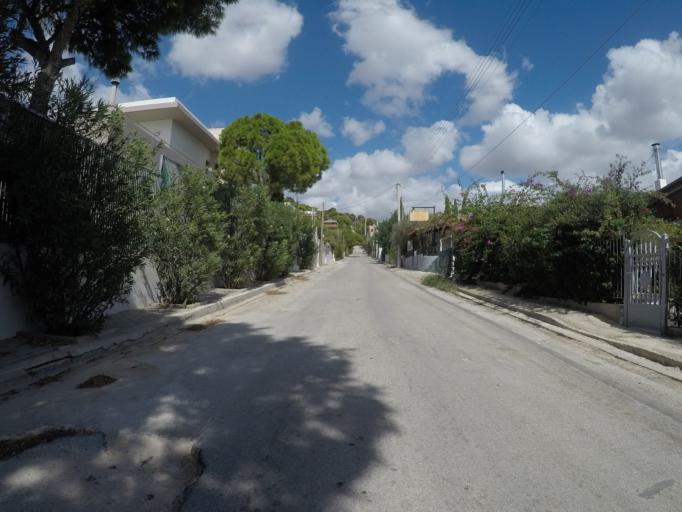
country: GR
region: Attica
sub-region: Nomarchia Anatolikis Attikis
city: Agios Dimitrios Kropias
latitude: 37.7989
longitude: 23.8735
